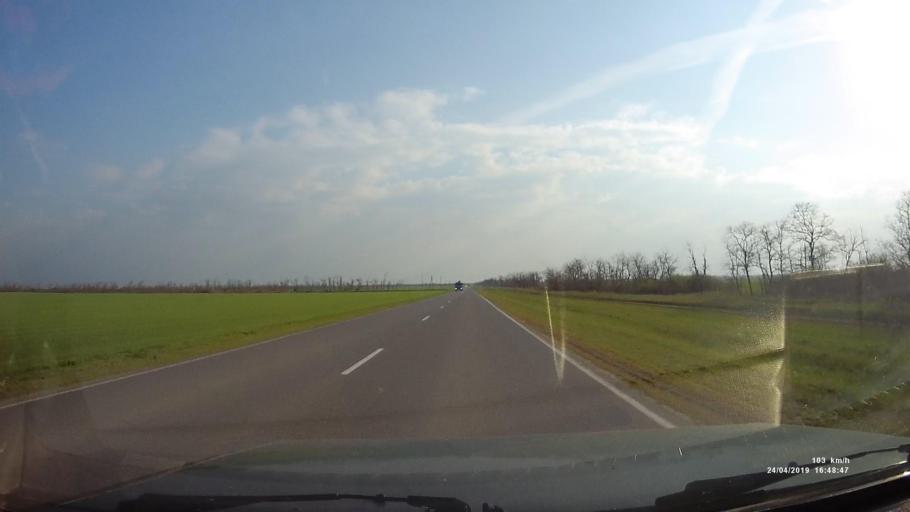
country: RU
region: Rostov
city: Proletarsk
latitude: 46.7262
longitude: 41.7714
